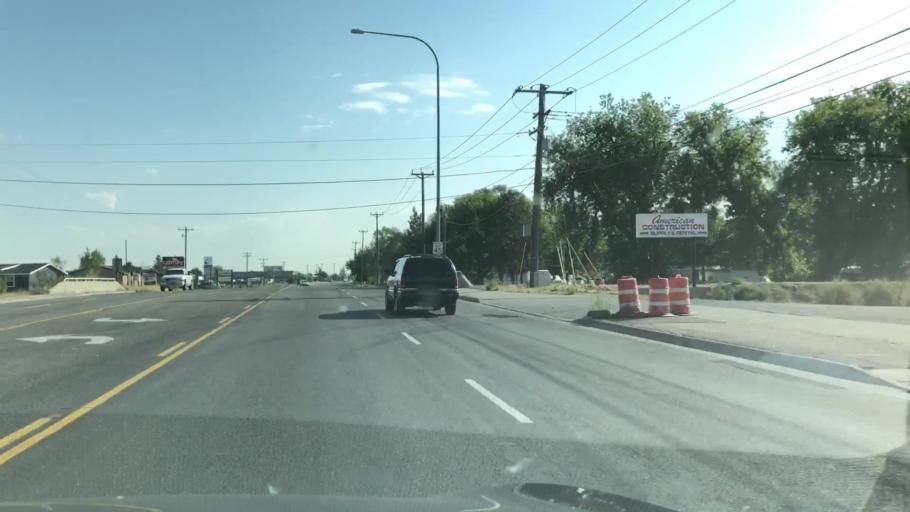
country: US
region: Idaho
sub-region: Bonneville County
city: Lincoln
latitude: 43.5150
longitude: -112.0093
